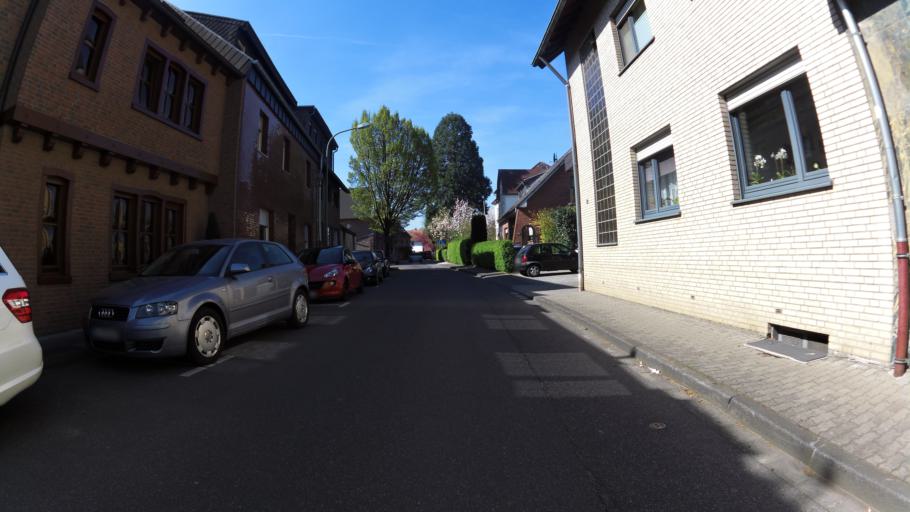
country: DE
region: North Rhine-Westphalia
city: Baesweiler
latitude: 50.9248
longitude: 6.1682
